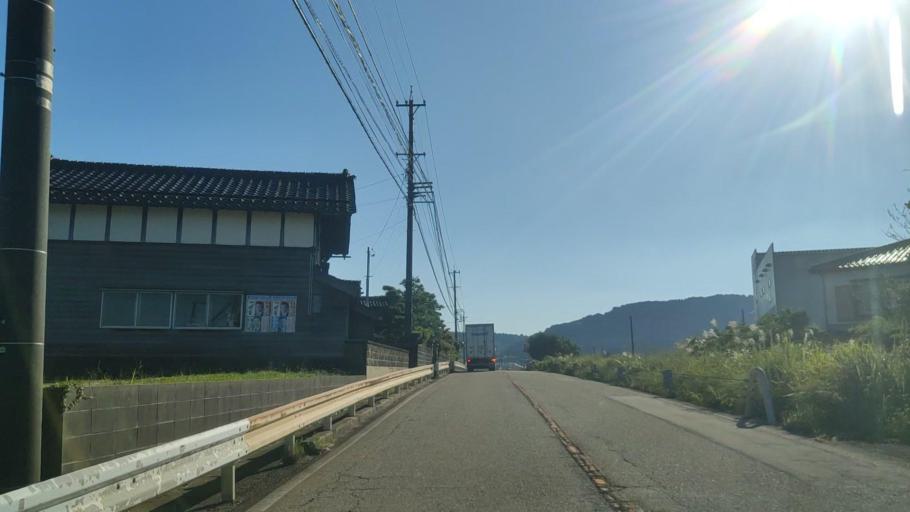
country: JP
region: Ishikawa
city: Nanao
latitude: 37.1498
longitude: 136.8773
